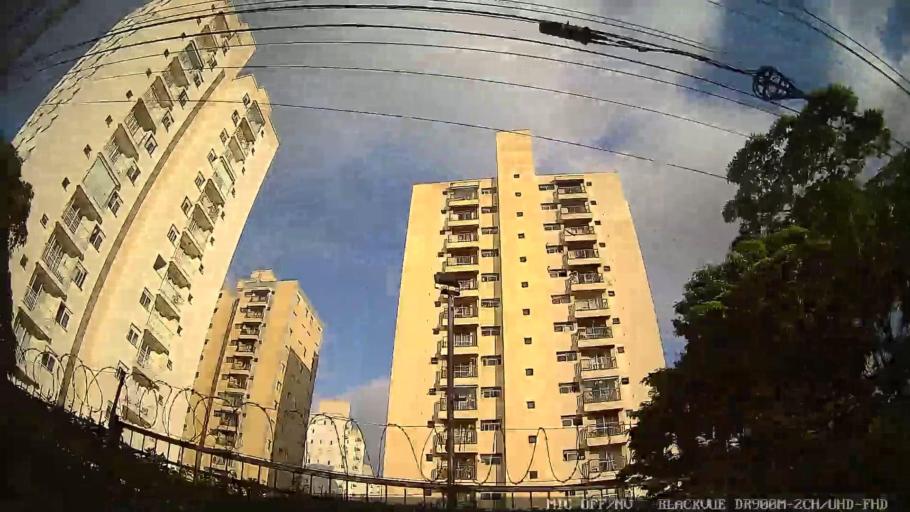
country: BR
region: Sao Paulo
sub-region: Taboao Da Serra
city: Taboao da Serra
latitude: -23.6161
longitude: -46.7566
